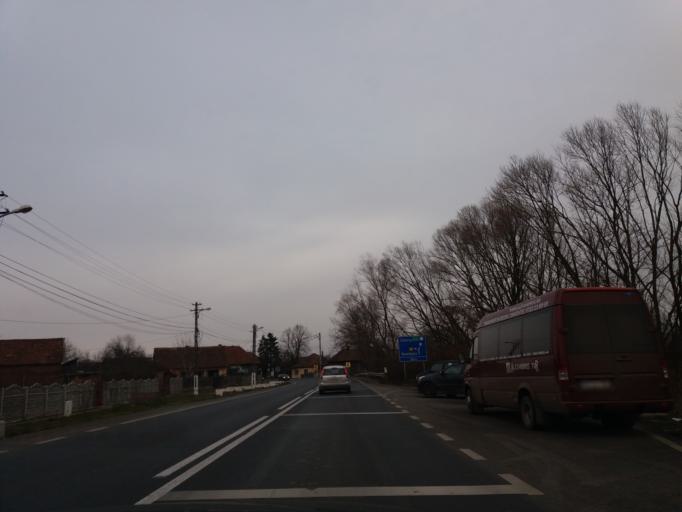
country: RO
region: Hunedoara
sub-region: Comuna Bacia
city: Bacia
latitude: 45.7733
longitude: 23.0024
